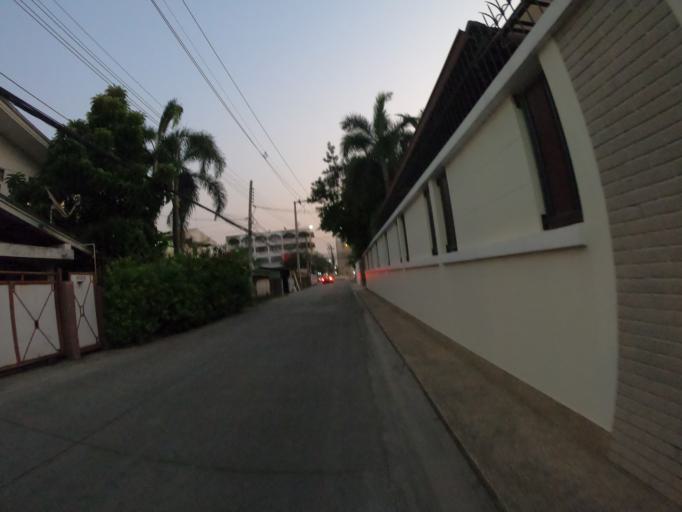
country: TH
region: Bangkok
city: Lat Phrao
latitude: 13.8266
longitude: 100.6207
